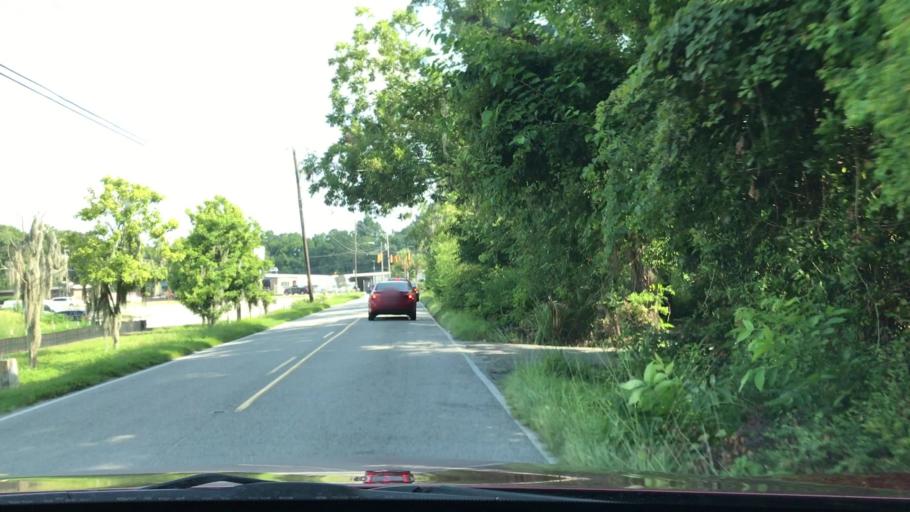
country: US
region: South Carolina
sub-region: Charleston County
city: Shell Point
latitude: 32.7906
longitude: -80.0275
